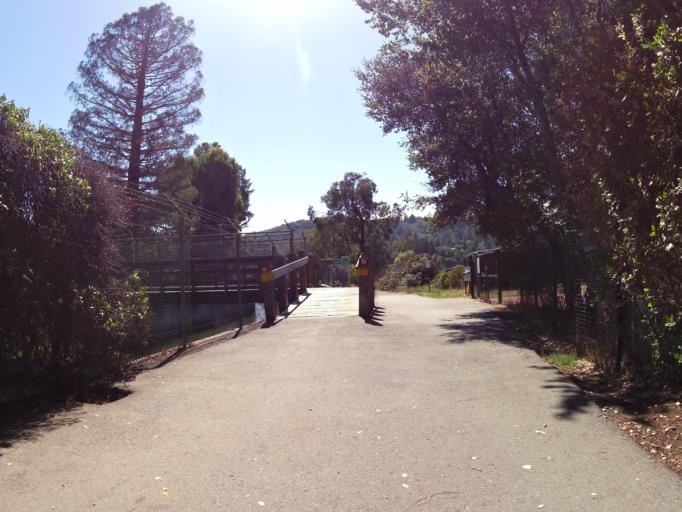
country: US
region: California
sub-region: Marin County
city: Kentfield
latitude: 37.9529
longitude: -122.5460
